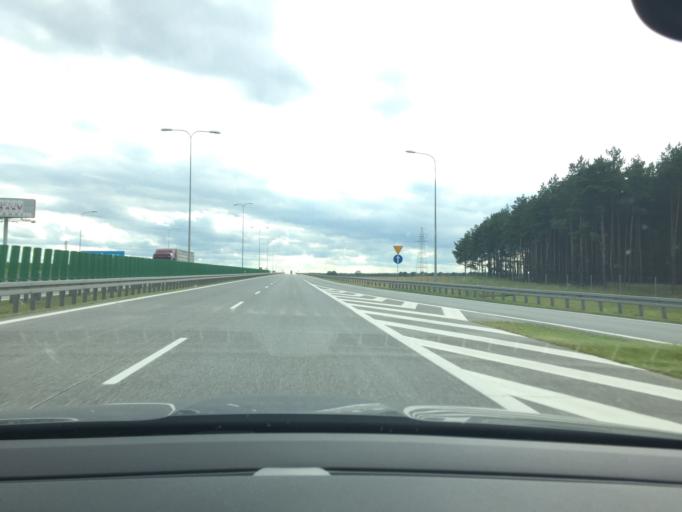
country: PL
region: Lubusz
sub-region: Powiat swiebodzinski
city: Zbaszynek
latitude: 52.3127
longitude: 15.7811
